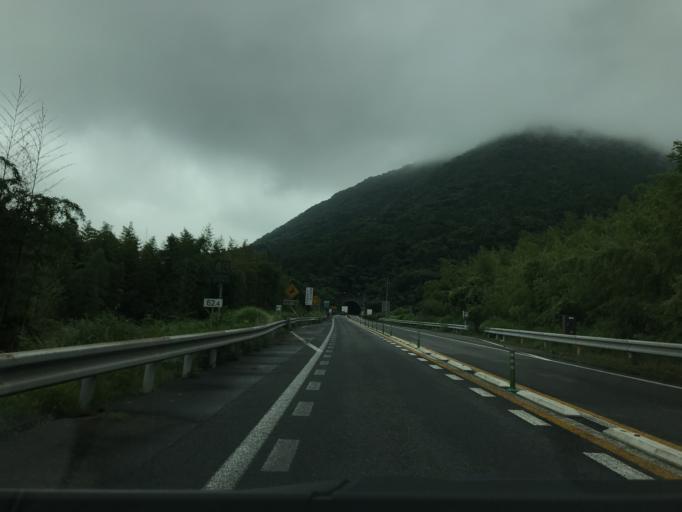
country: JP
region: Oita
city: Bungo-Takada-shi
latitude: 33.4907
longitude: 131.3227
